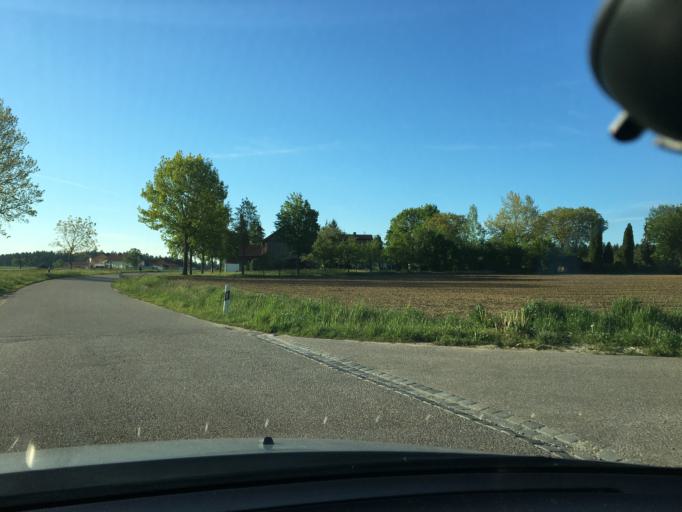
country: DE
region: Bavaria
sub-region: Lower Bavaria
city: Vilsbiburg
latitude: 48.4911
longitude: 12.3742
